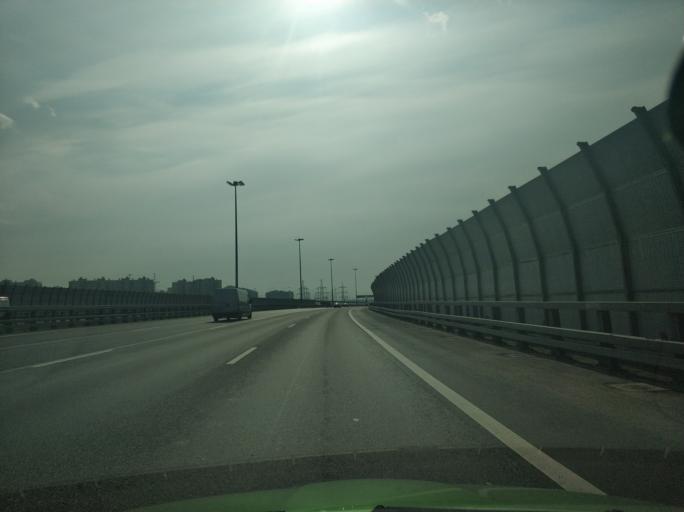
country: RU
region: Leningrad
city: Murino
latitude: 60.0413
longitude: 30.4377
